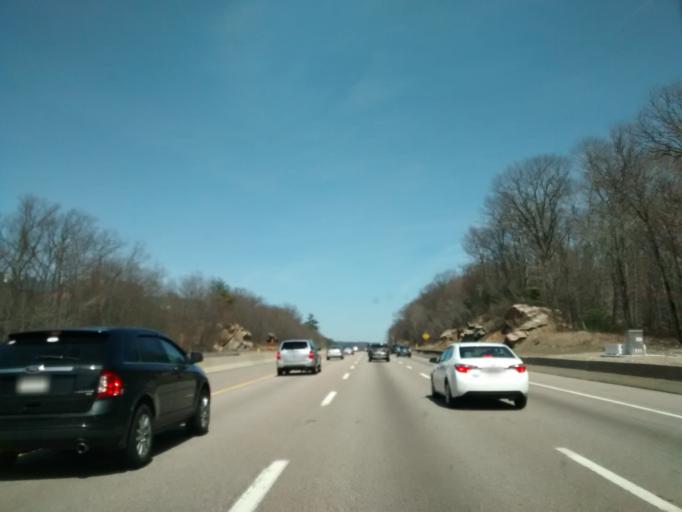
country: US
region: Massachusetts
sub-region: Worcester County
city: Southborough
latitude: 42.2890
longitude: -71.4902
